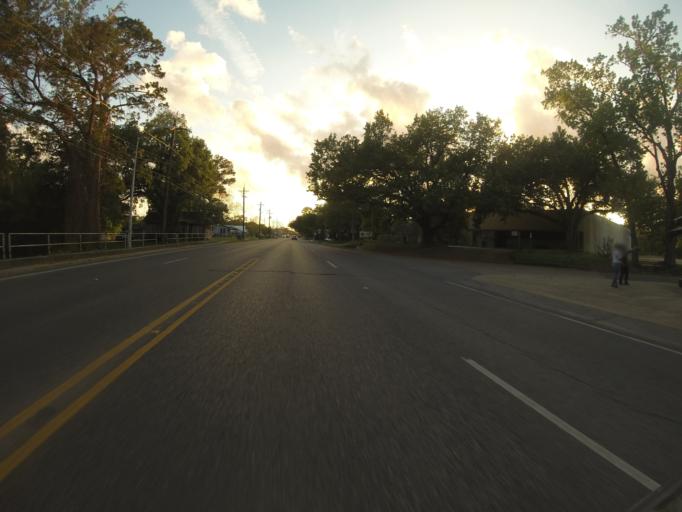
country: US
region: Louisiana
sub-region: Lafayette Parish
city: Lafayette
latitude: 30.2137
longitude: -92.0229
